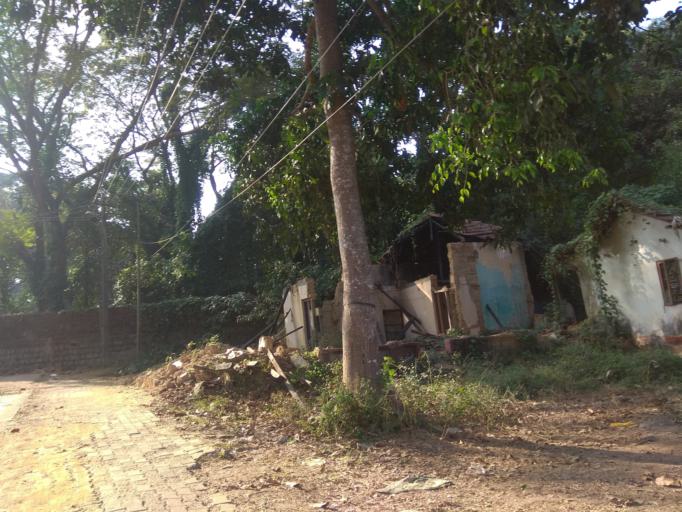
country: IN
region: Karnataka
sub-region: Dakshina Kannada
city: Ullal
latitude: 12.8458
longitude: 74.8541
